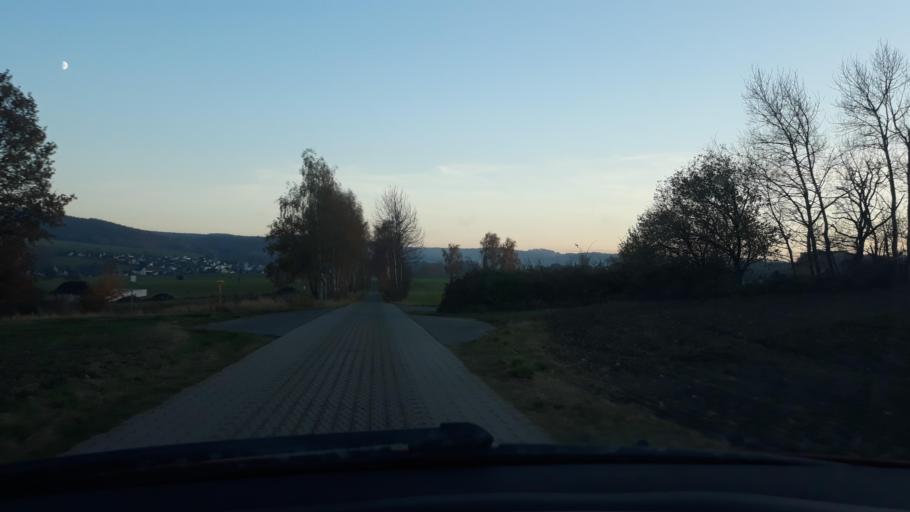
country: DE
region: Saxony
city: Kirchberg
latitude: 50.6084
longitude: 12.5362
